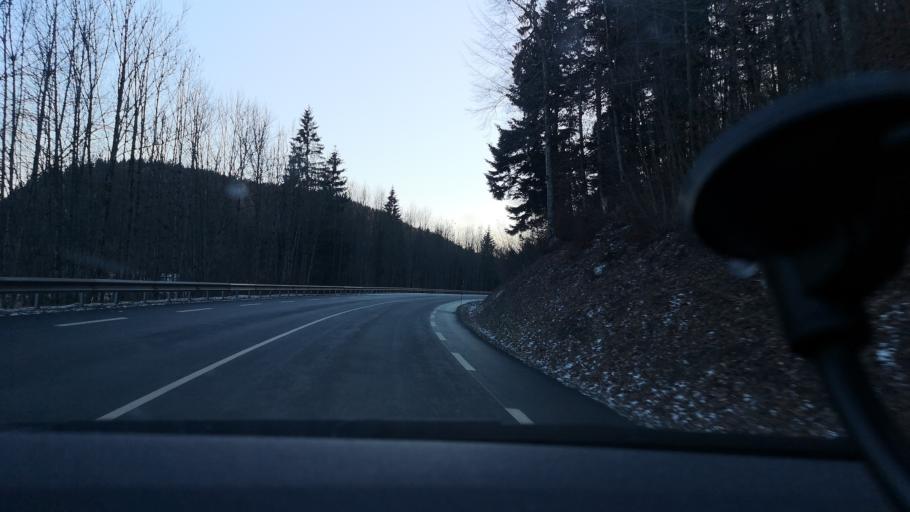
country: FR
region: Franche-Comte
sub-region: Departement du Doubs
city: La Cluse-et-Mijoux
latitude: 46.8699
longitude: 6.3641
